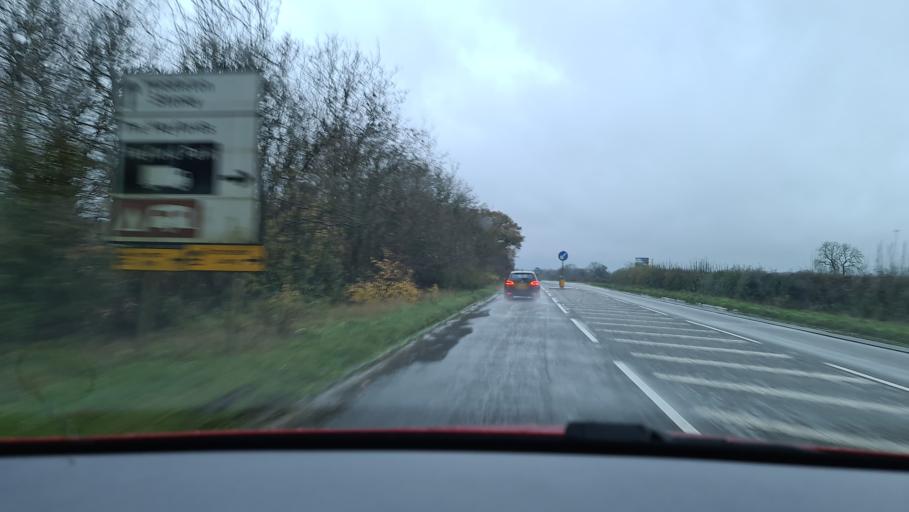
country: GB
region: England
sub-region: Oxfordshire
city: Somerton
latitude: 51.9274
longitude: -1.2187
